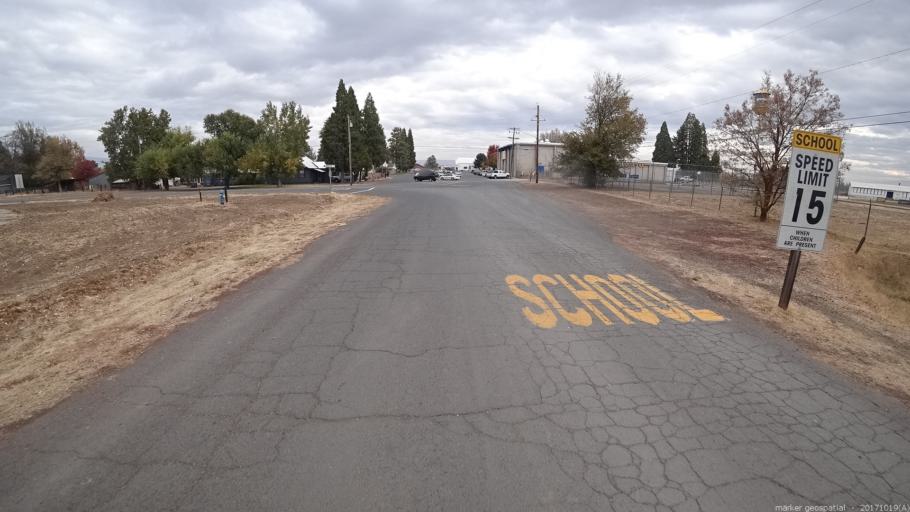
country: US
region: California
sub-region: Shasta County
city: Burney
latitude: 41.0464
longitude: -121.4010
